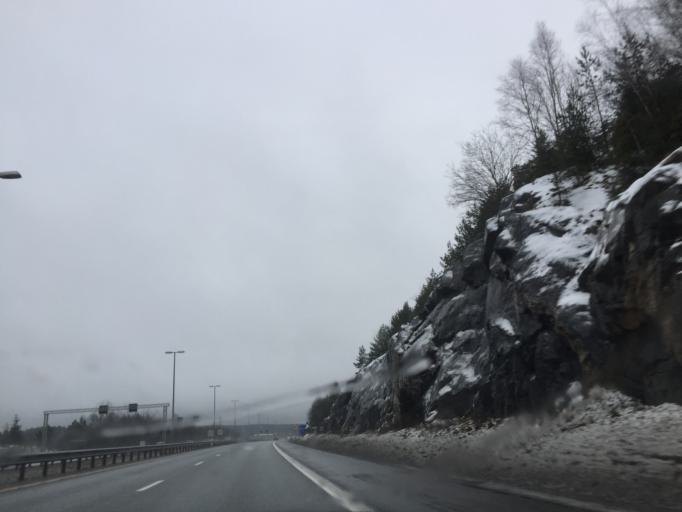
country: NO
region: Akershus
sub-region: Vestby
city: Vestby
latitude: 59.5243
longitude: 10.7290
